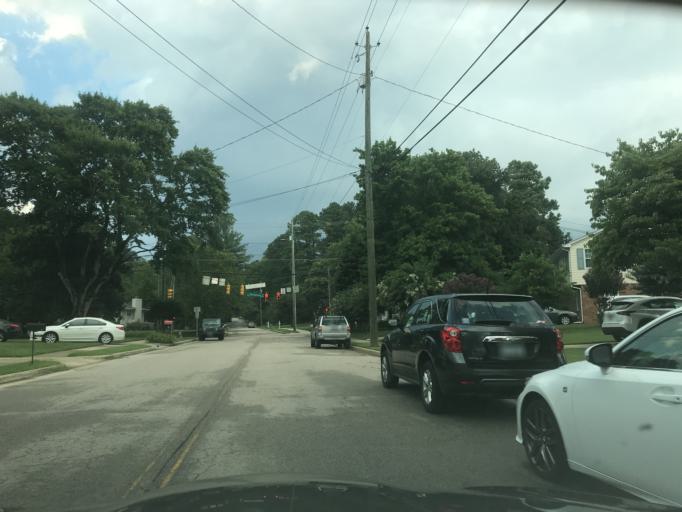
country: US
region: North Carolina
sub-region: Wake County
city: West Raleigh
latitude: 35.8439
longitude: -78.6516
